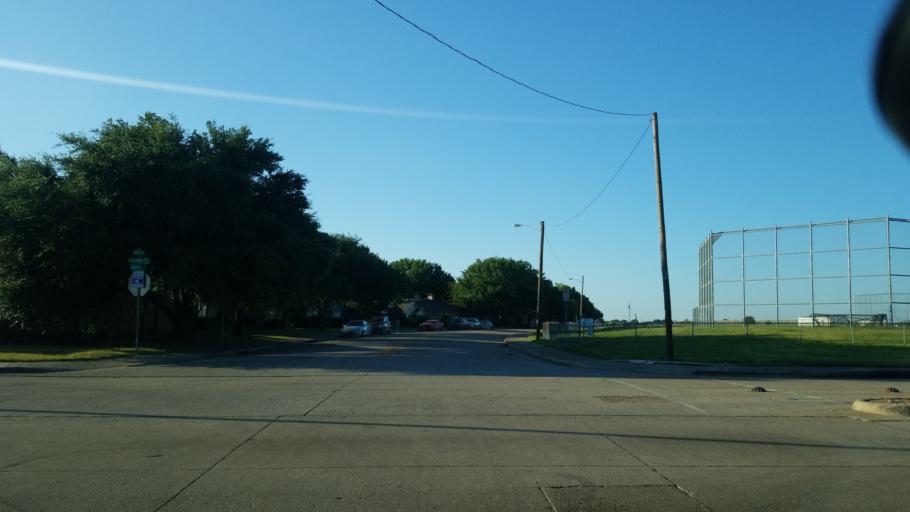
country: US
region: Texas
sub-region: Dallas County
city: Balch Springs
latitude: 32.7779
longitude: -96.6943
